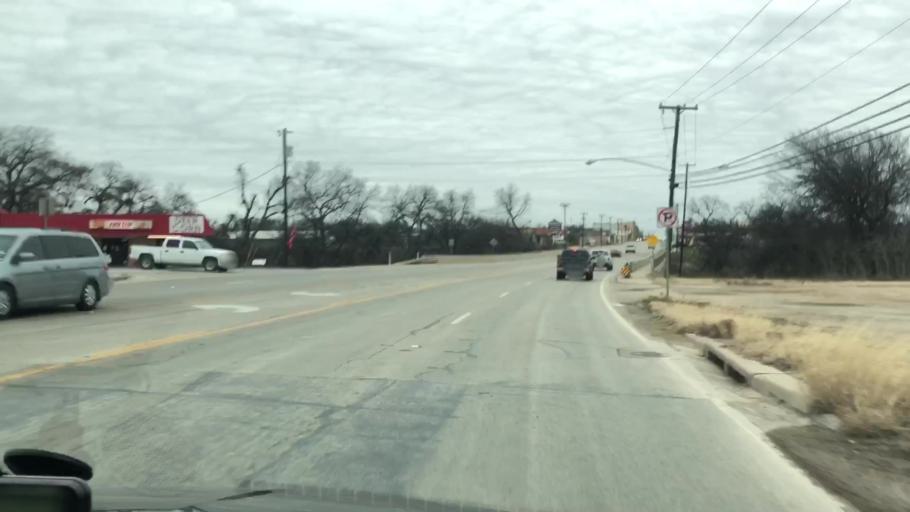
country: US
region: Texas
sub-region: Jack County
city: Jacksboro
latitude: 33.2126
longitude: -98.1587
